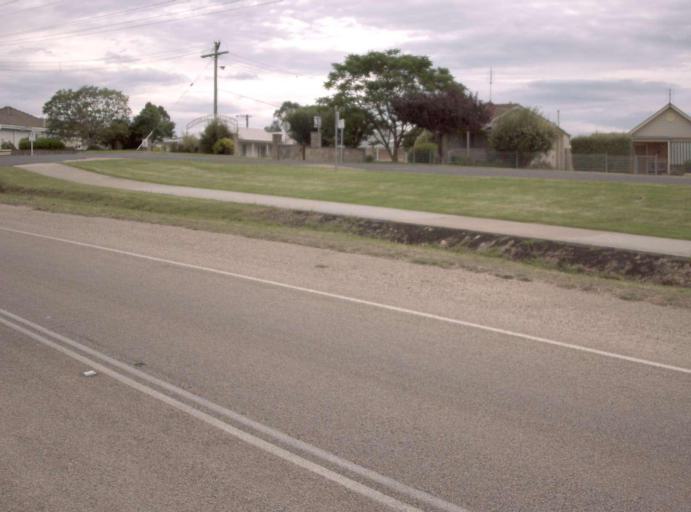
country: AU
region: Victoria
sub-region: East Gippsland
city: Bairnsdale
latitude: -37.8090
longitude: 147.6192
